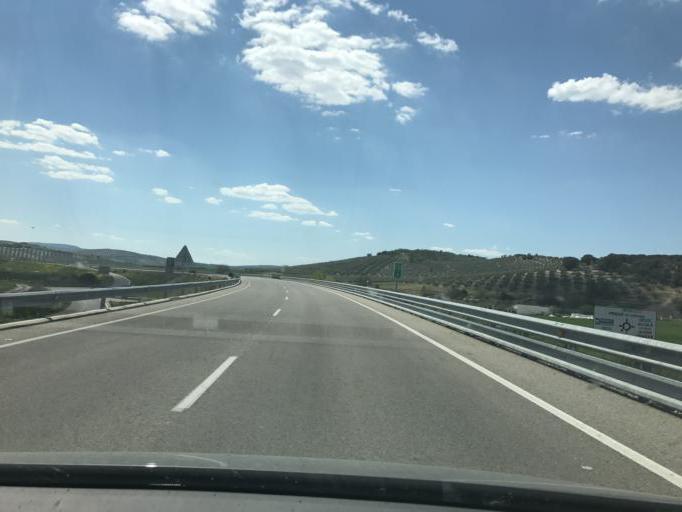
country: ES
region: Andalusia
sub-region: Provincia de Jaen
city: Alcala la Real
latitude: 37.4519
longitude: -3.8895
